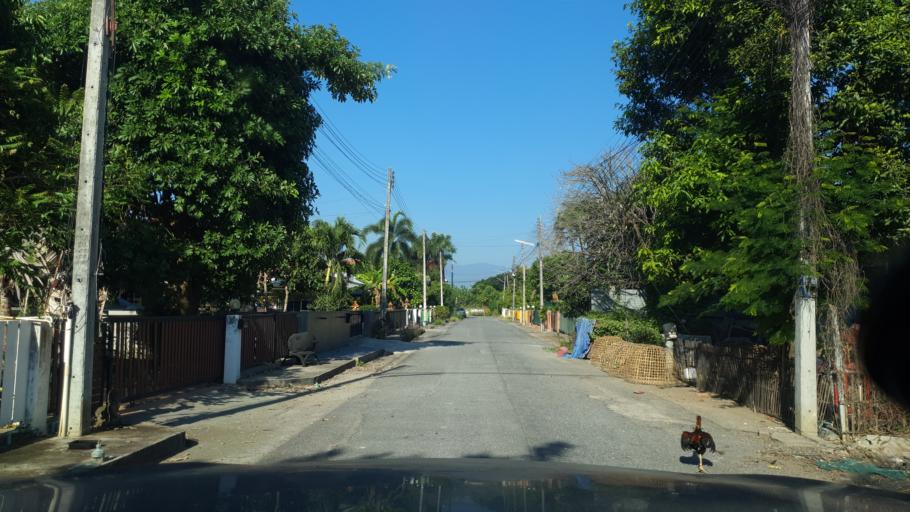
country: TH
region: Chiang Mai
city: Saraphi
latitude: 18.7252
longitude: 99.0603
